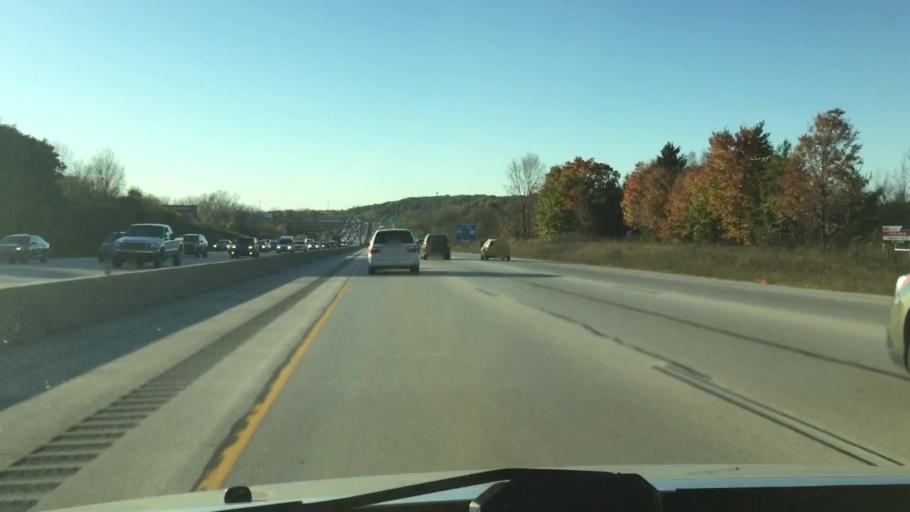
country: US
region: Wisconsin
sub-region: Waukesha County
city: Waukesha
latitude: 43.0443
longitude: -88.1945
